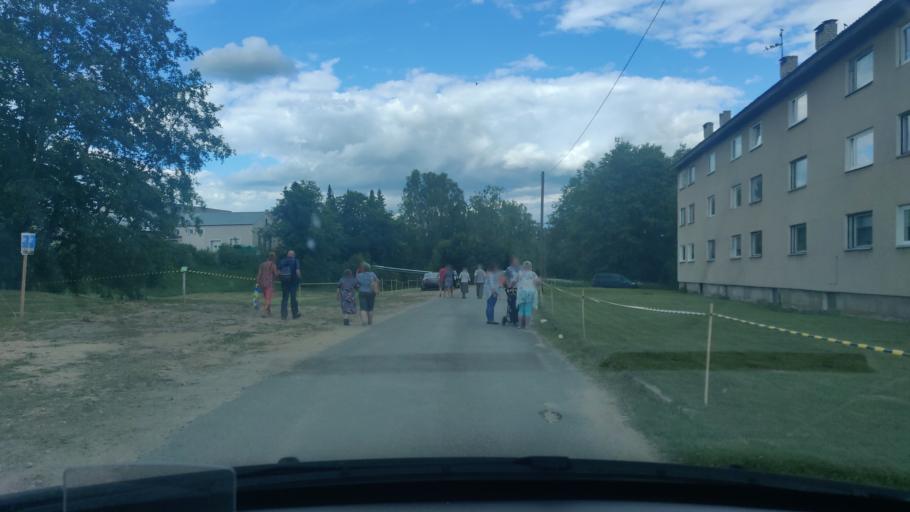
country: EE
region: Jogevamaa
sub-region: Mustvee linn
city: Mustvee
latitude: 58.9856
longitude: 26.8733
